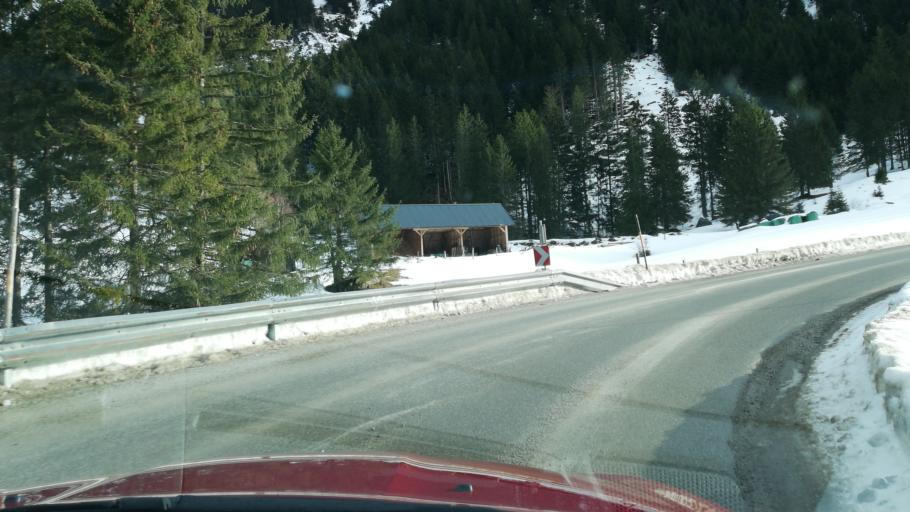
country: AT
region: Styria
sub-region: Politischer Bezirk Liezen
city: Donnersbach
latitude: 47.4176
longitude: 14.1732
